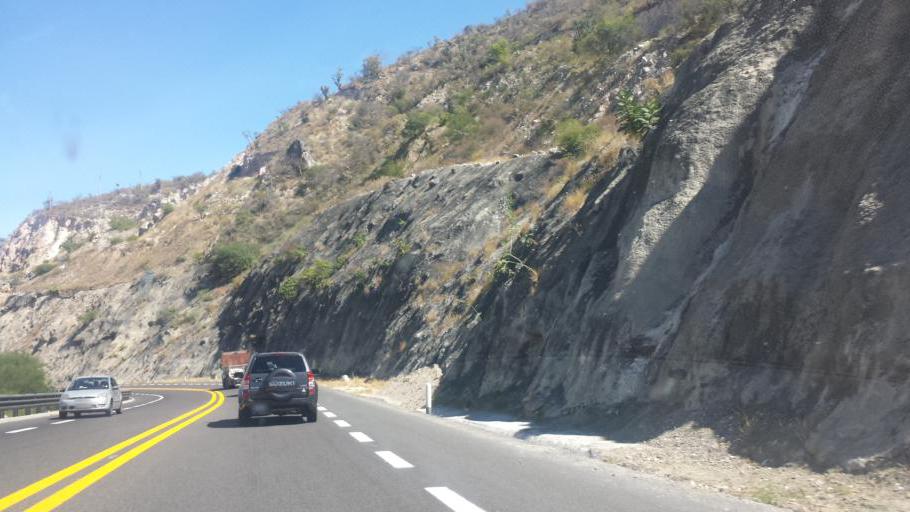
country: MX
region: Puebla
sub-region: San Jose Miahuatlan
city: San Pedro Tetitlan
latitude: 18.1413
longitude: -97.3156
